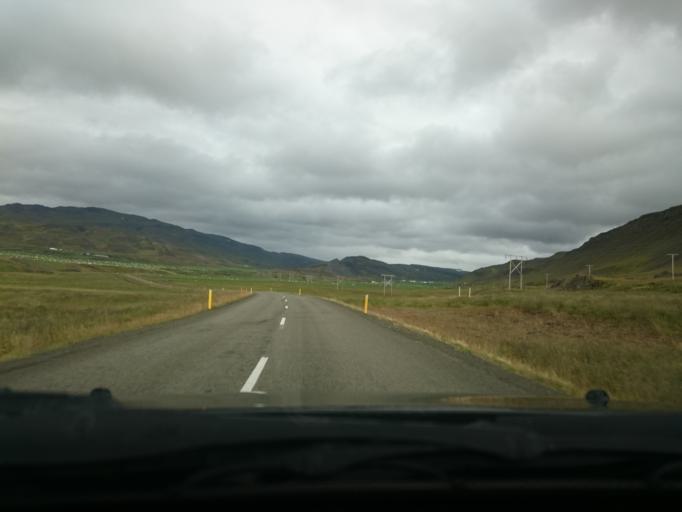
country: IS
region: West
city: Stykkisholmur
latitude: 65.4612
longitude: -21.9136
